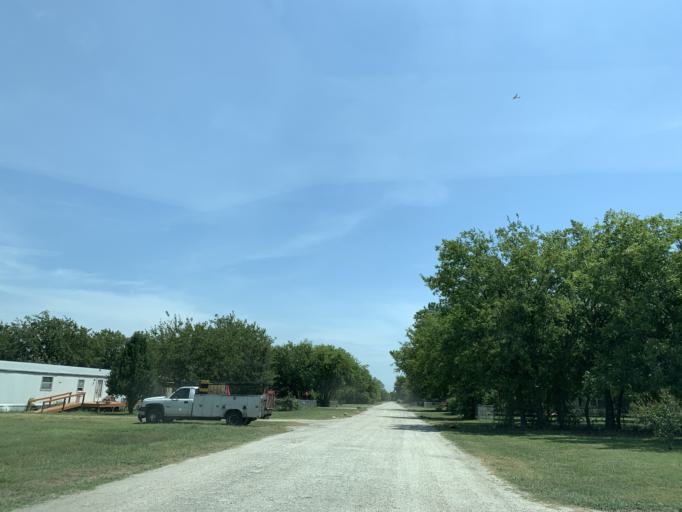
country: US
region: Texas
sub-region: Dallas County
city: Cedar Hill
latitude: 32.6423
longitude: -97.0297
